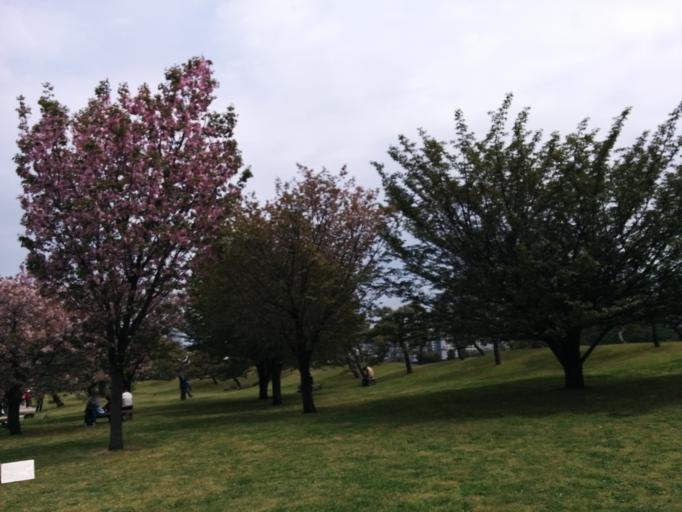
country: JP
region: Tokyo
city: Tokyo
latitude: 35.6576
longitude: 139.7633
